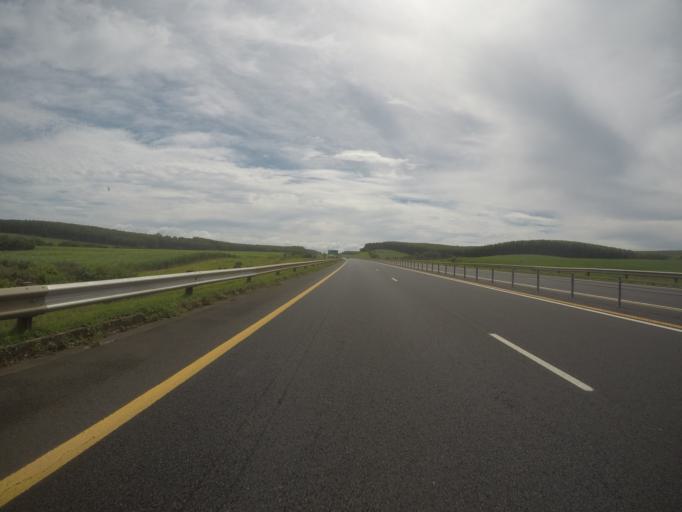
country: ZA
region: KwaZulu-Natal
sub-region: uThungulu District Municipality
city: Eshowe
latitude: -29.0472
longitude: 31.6421
